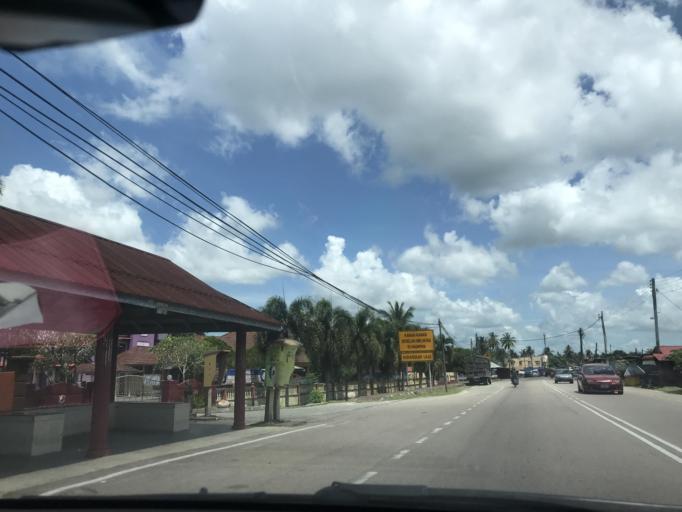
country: MY
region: Kelantan
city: Tumpat
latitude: 6.2182
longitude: 102.1176
